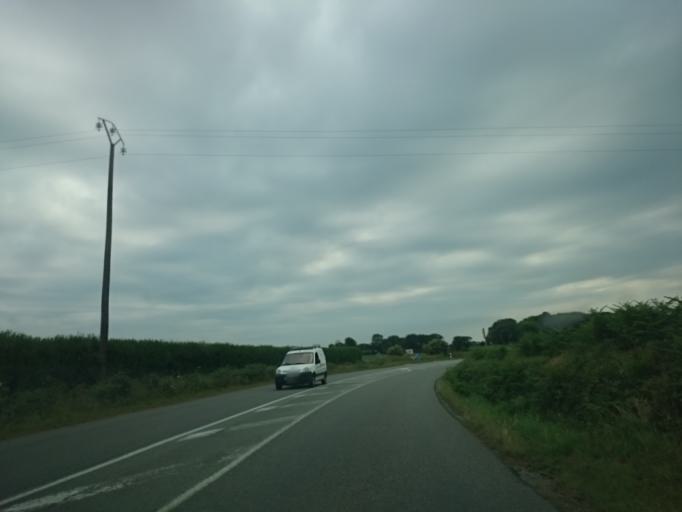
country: FR
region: Brittany
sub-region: Departement du Finistere
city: Ploumoguer
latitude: 48.3981
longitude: -4.6693
